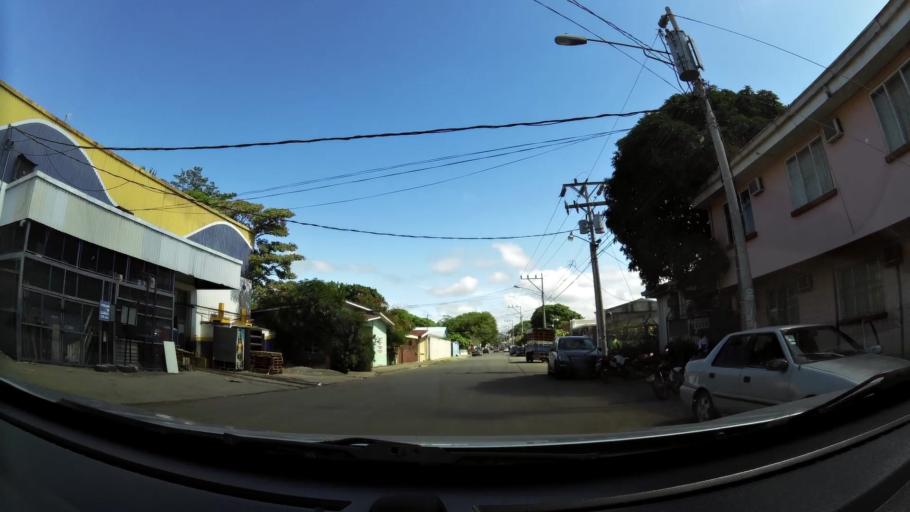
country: CR
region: Guanacaste
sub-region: Canton de Canas
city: Canas
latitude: 10.4267
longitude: -85.0939
